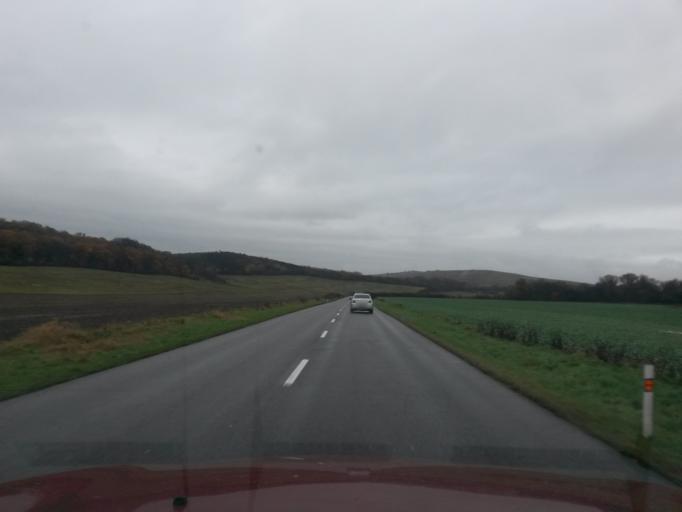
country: SK
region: Kosicky
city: Kosice
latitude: 48.6487
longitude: 21.3751
